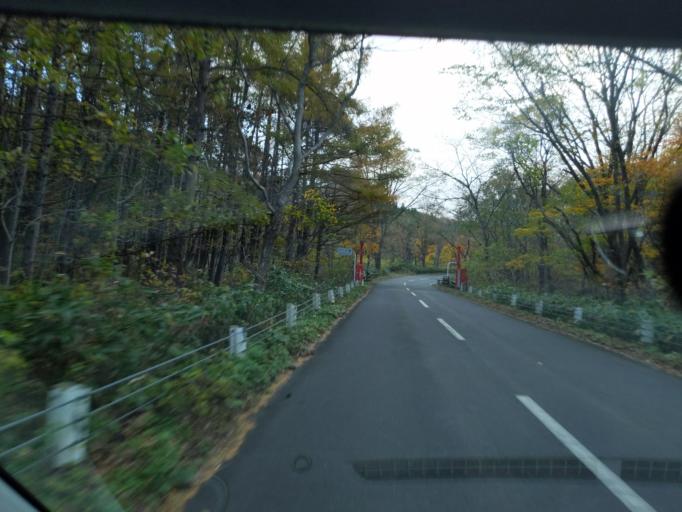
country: JP
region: Iwate
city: Mizusawa
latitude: 39.1140
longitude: 140.8802
